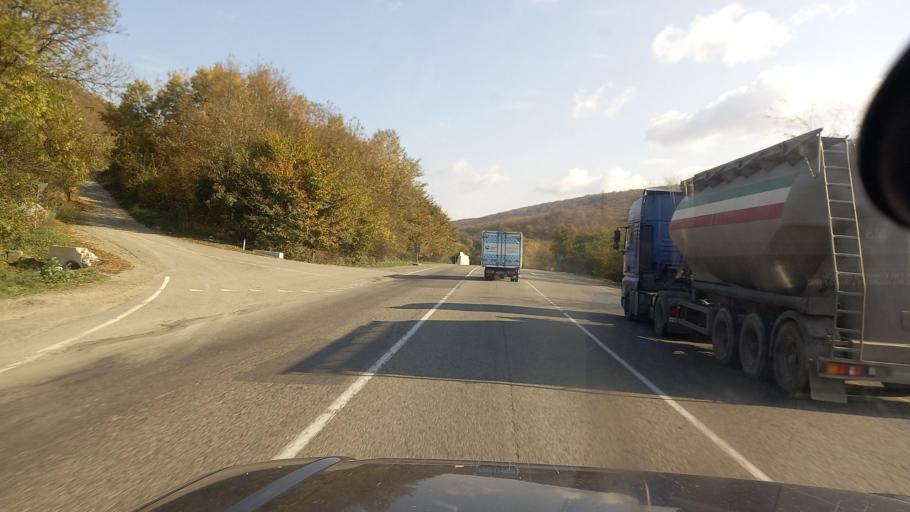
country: RU
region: Krasnodarskiy
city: Verkhnebakanskiy
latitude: 44.8426
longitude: 37.7136
